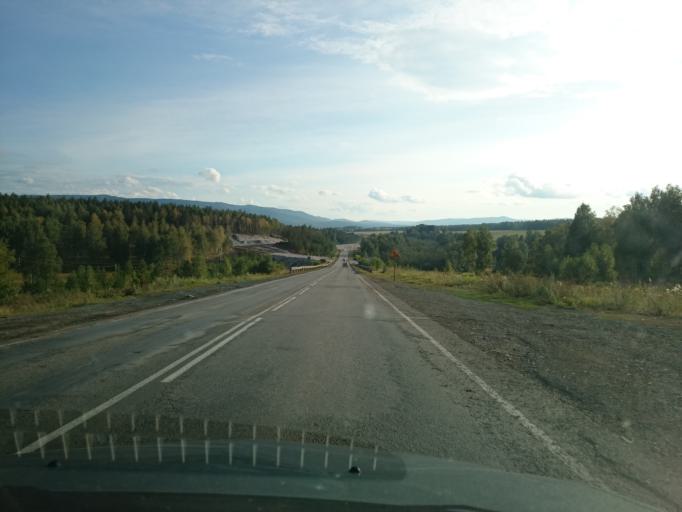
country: RU
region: Bashkortostan
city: Lomovka
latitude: 53.9145
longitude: 58.1842
